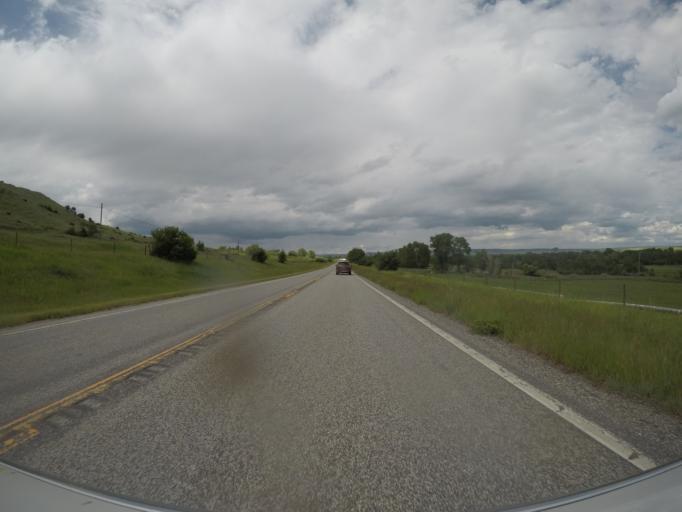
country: US
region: Montana
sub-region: Sweet Grass County
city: Big Timber
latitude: 45.8182
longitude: -109.9558
